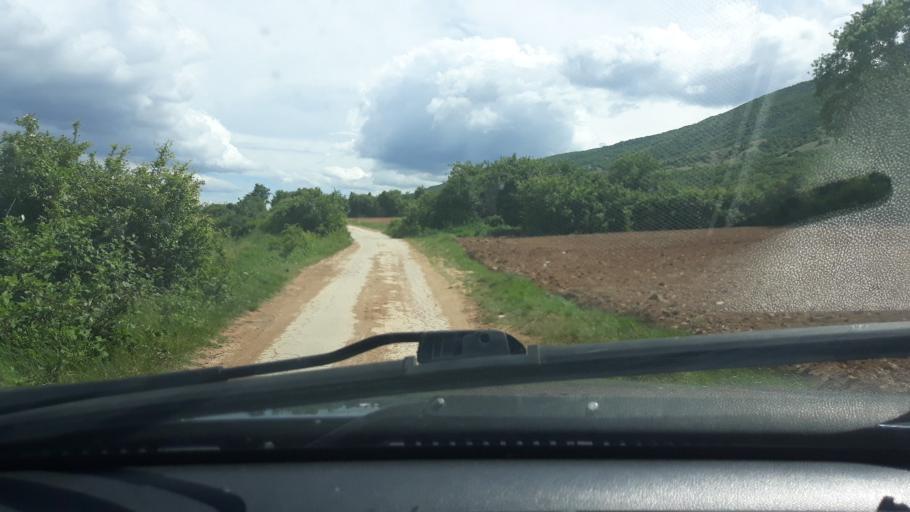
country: MK
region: Krivogastani
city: Krivogashtani
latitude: 41.3361
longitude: 21.3010
